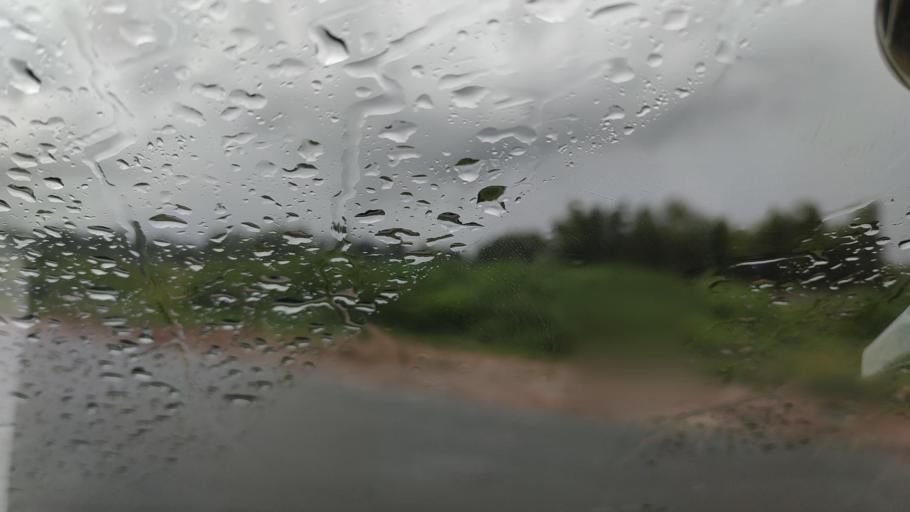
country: MM
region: Bago
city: Bago
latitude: 17.5670
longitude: 96.5466
